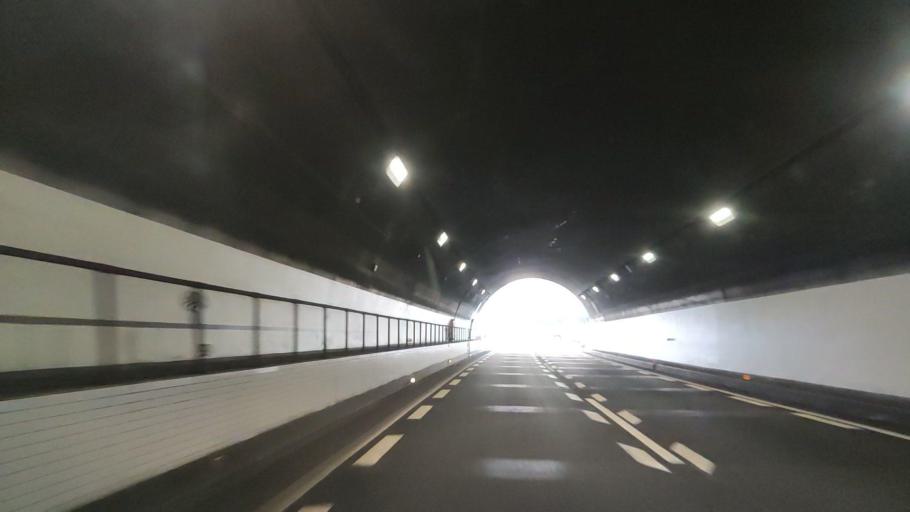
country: JP
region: Hiroshima
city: Fukuyama
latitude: 34.5122
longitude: 133.3420
